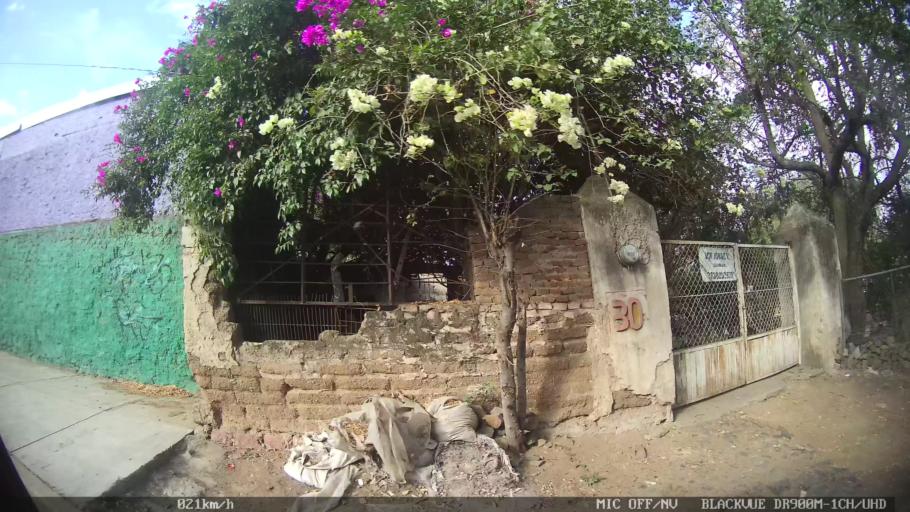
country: MX
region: Jalisco
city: Tonala
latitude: 20.6793
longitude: -103.2471
